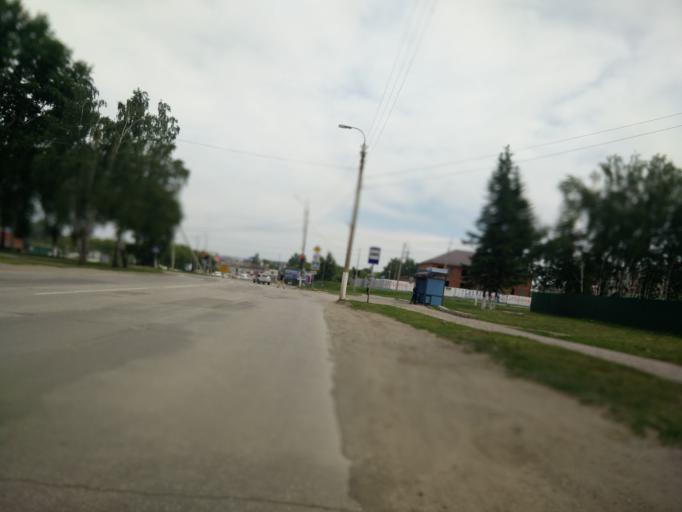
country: RU
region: Novosibirsk
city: Berdsk
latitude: 54.7549
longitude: 83.1217
